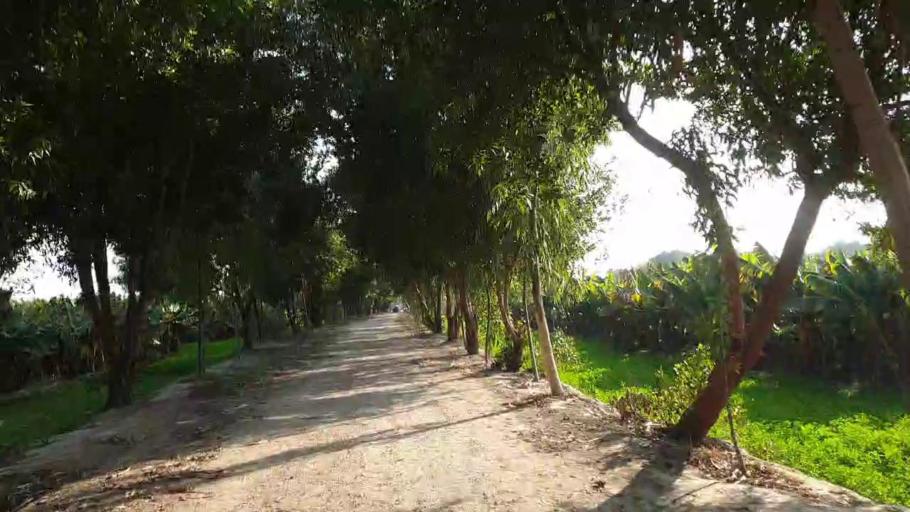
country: PK
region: Sindh
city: Matiari
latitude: 25.6314
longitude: 68.5872
